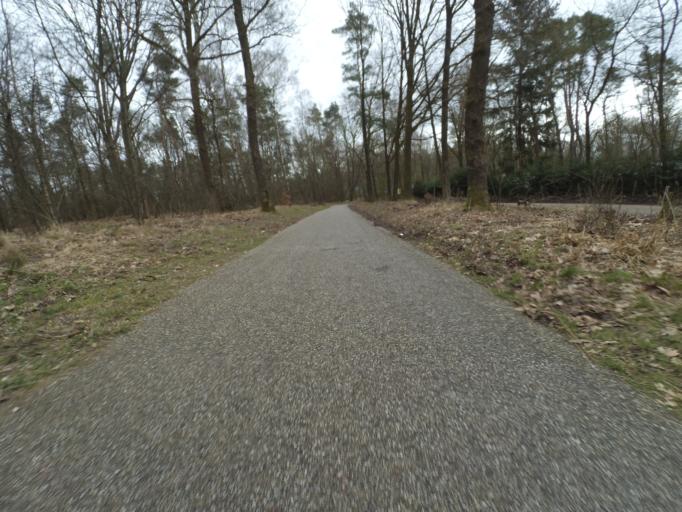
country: NL
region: Gelderland
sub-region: Gemeente Apeldoorn
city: Beekbergen
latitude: 52.1233
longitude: 5.9292
